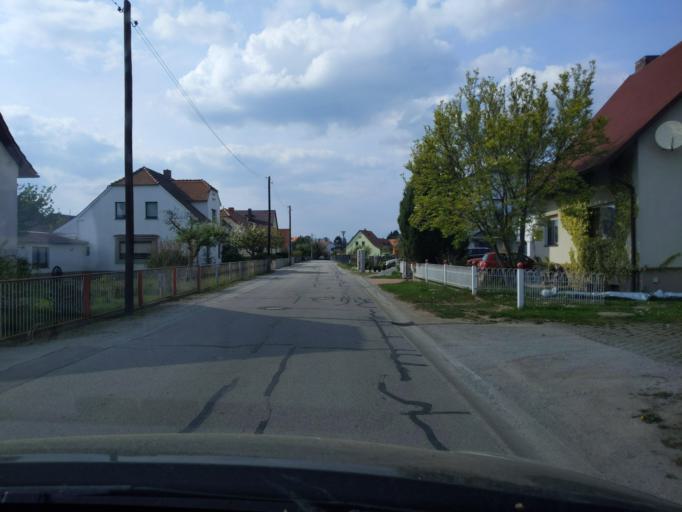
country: DE
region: Saxony
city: Malschwitz
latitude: 51.2352
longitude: 14.5253
